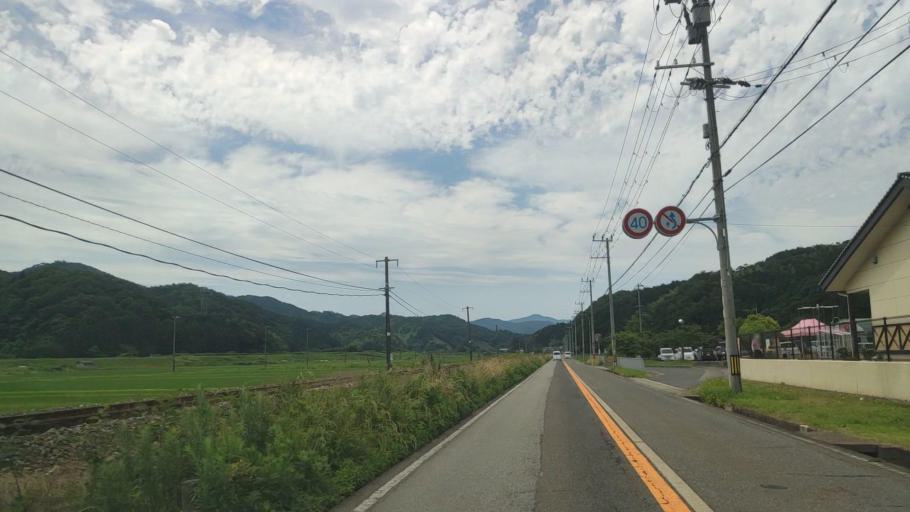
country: JP
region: Hyogo
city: Toyooka
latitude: 35.6407
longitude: 134.7580
